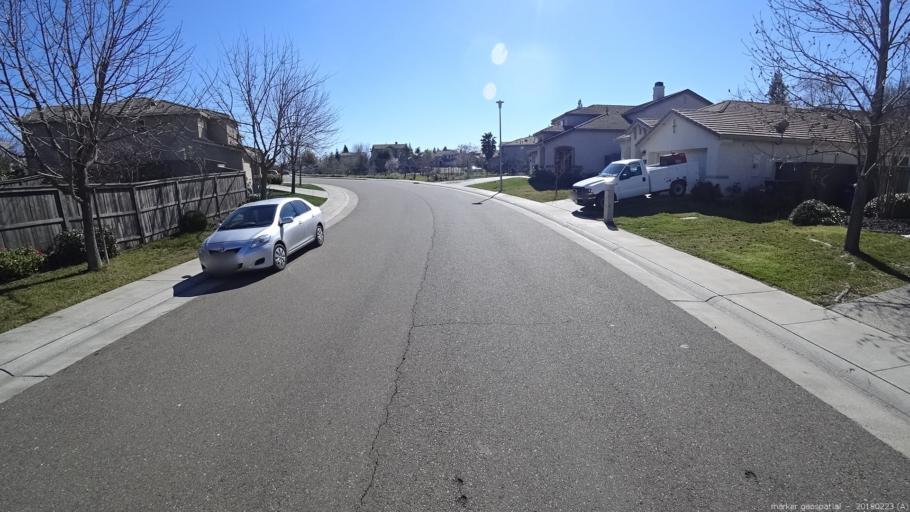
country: US
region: California
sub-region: Sacramento County
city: Antelope
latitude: 38.7057
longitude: -121.3548
